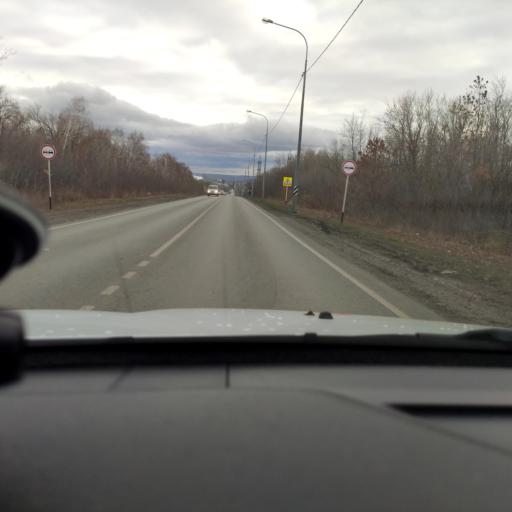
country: RU
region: Samara
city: Petra-Dubrava
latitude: 53.2790
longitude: 50.3794
